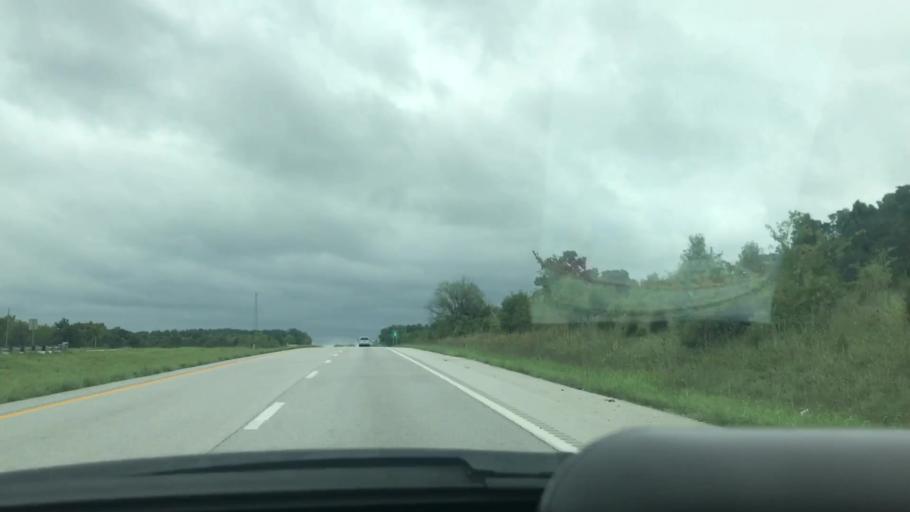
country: US
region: Missouri
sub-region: Greene County
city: Fair Grove
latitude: 37.4171
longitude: -93.1451
